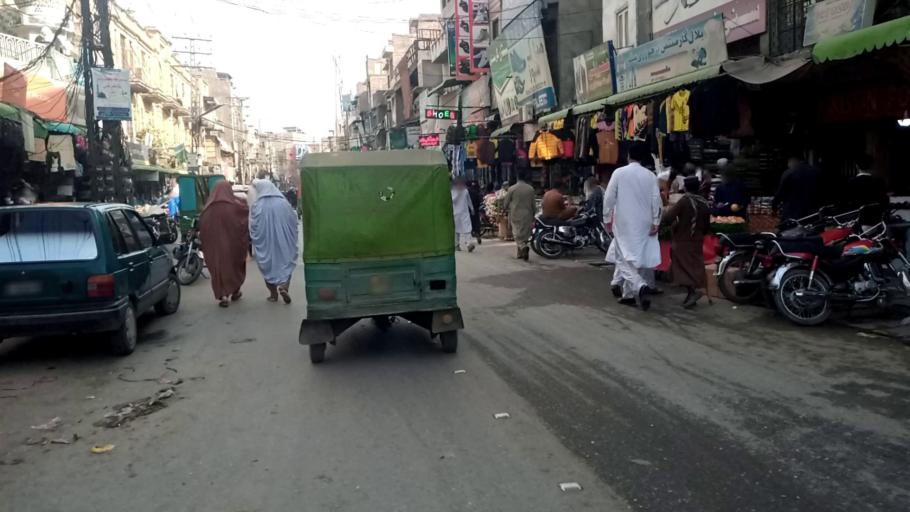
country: PK
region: Khyber Pakhtunkhwa
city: Peshawar
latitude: 34.0083
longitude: 71.5690
